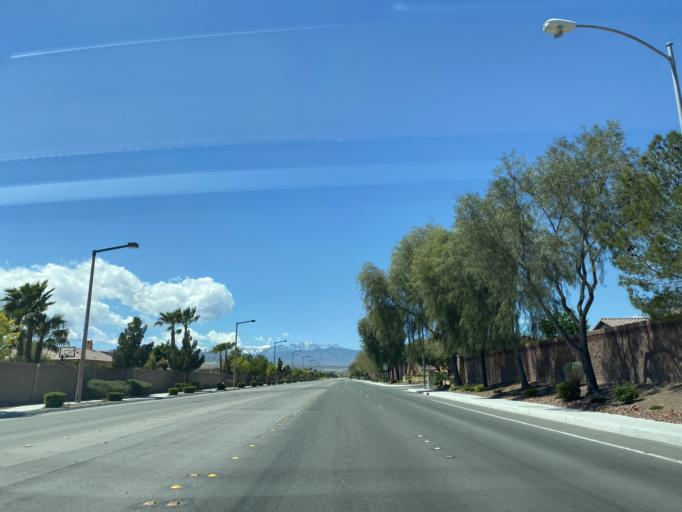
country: US
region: Nevada
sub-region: Clark County
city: North Las Vegas
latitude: 36.3127
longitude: -115.2268
